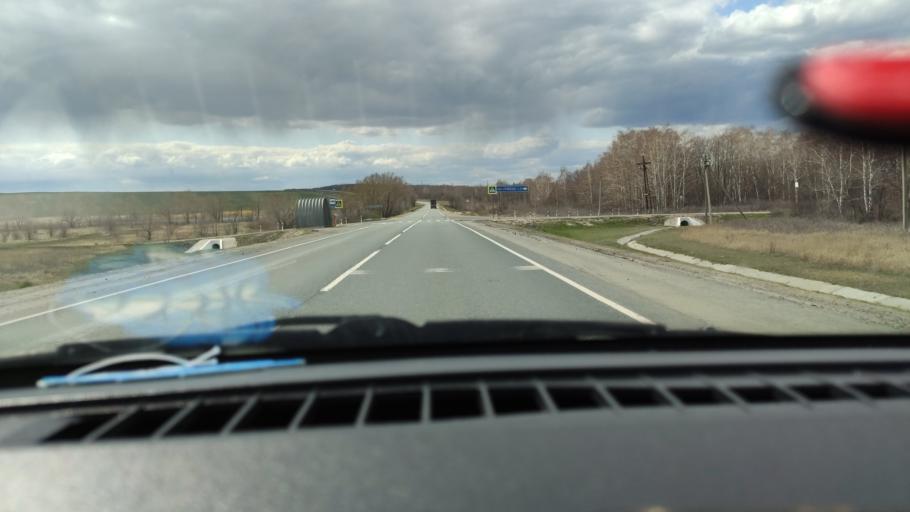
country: RU
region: Saratov
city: Alekseyevka
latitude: 52.2439
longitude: 47.9069
